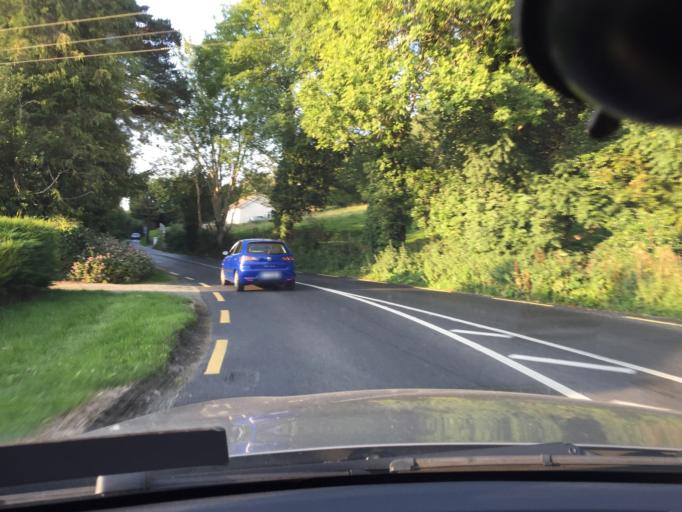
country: IE
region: Leinster
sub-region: Wicklow
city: Rathdrum
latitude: 53.0317
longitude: -6.2510
